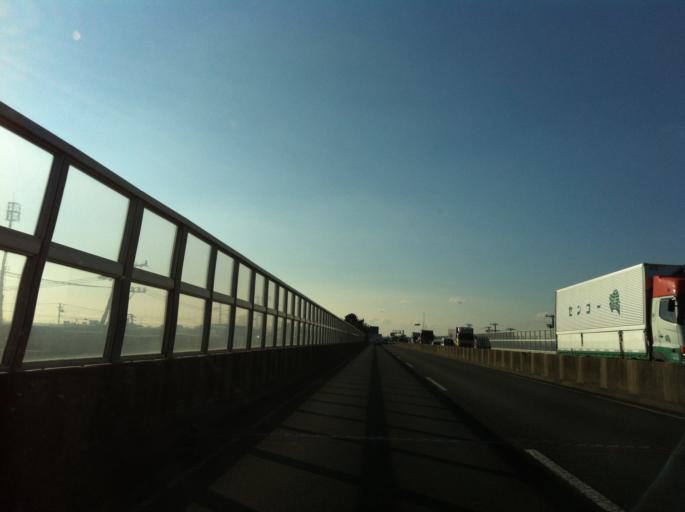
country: JP
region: Aichi
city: Kozakai-cho
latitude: 34.7734
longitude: 137.3325
